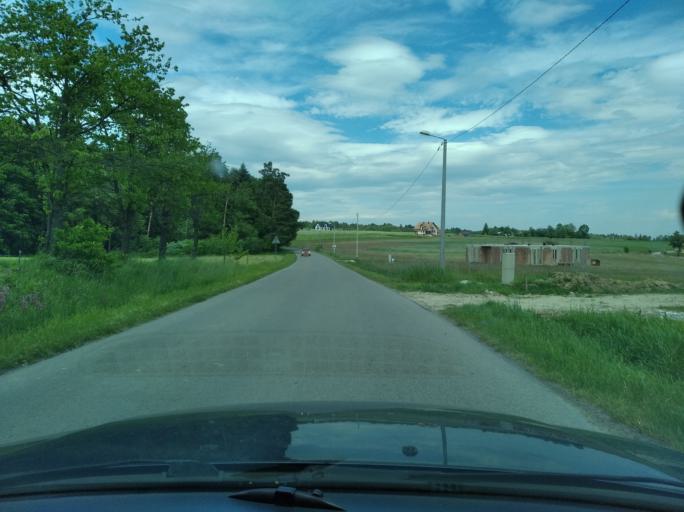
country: PL
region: Subcarpathian Voivodeship
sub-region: Powiat ropczycko-sedziszowski
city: Ropczyce
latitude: 50.0031
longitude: 21.6141
